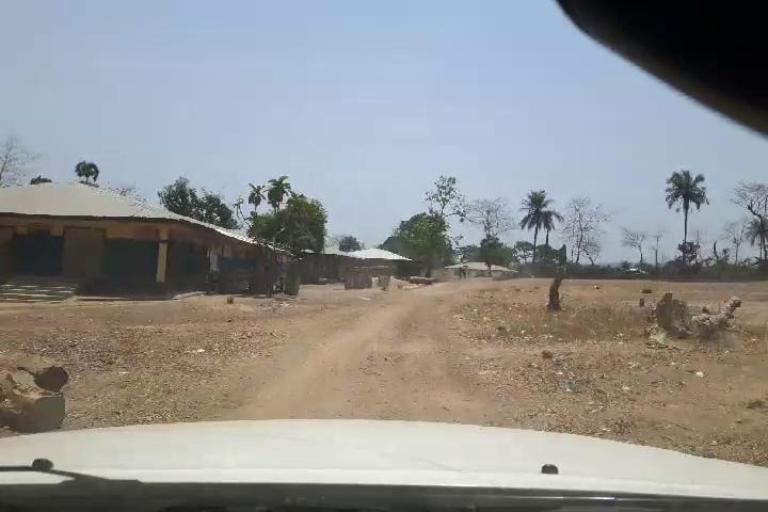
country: SL
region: Northern Province
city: Alikalia
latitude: 9.0641
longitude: -11.4852
